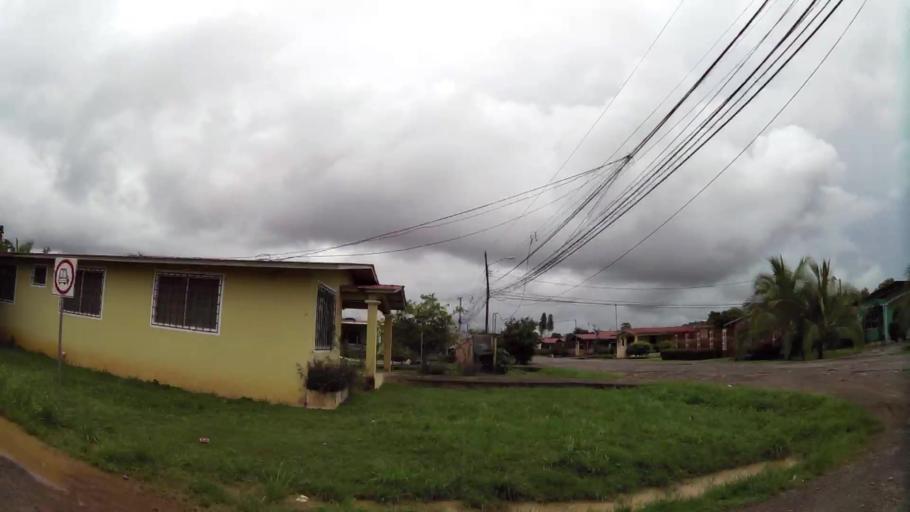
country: PA
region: Chiriqui
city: David
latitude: 8.4154
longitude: -82.4573
